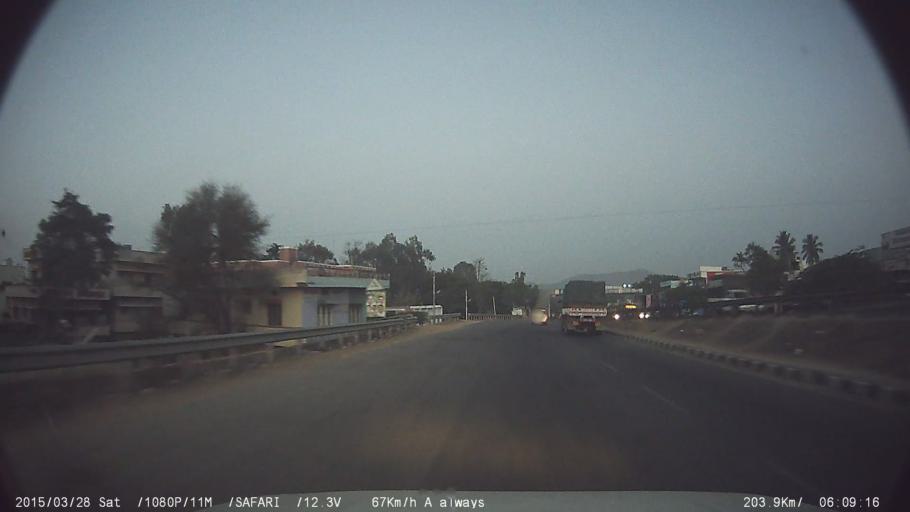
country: IN
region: Karnataka
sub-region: Ramanagara
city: Ramanagaram
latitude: 12.7966
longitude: 77.3871
